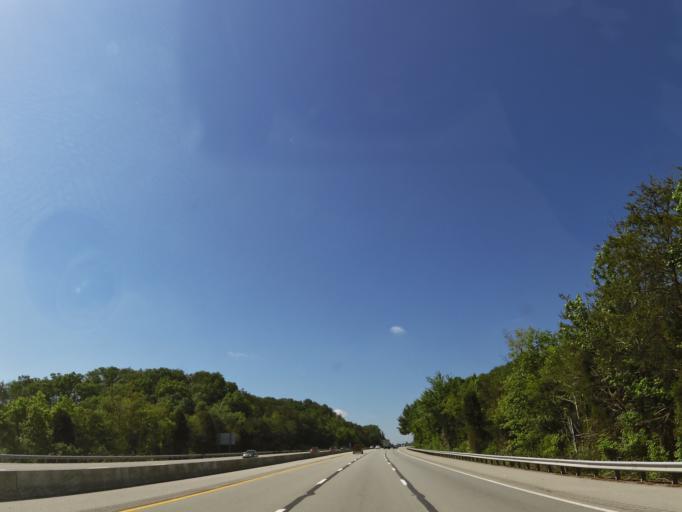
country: US
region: Kentucky
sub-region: Madison County
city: Berea
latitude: 37.5482
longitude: -84.3173
